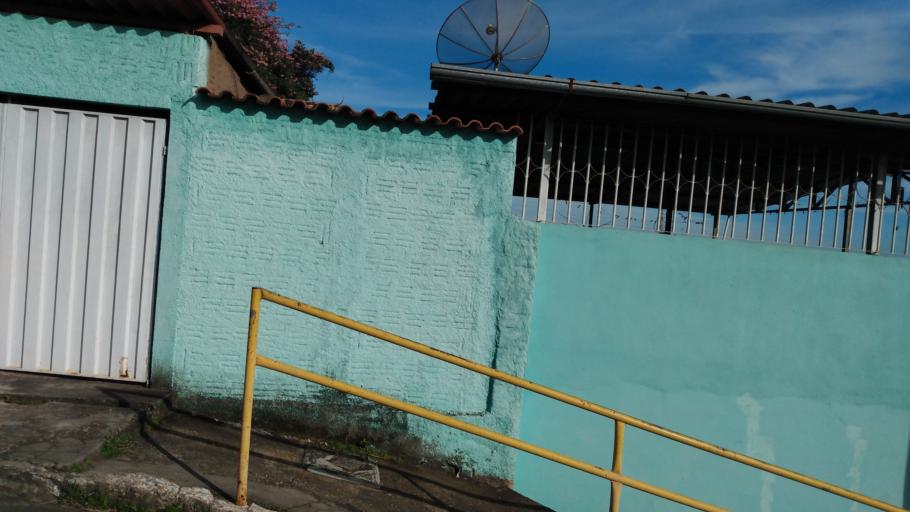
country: BR
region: Minas Gerais
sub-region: Sao Joao Del Rei
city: Sao Joao del Rei
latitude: -21.1428
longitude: -44.2571
